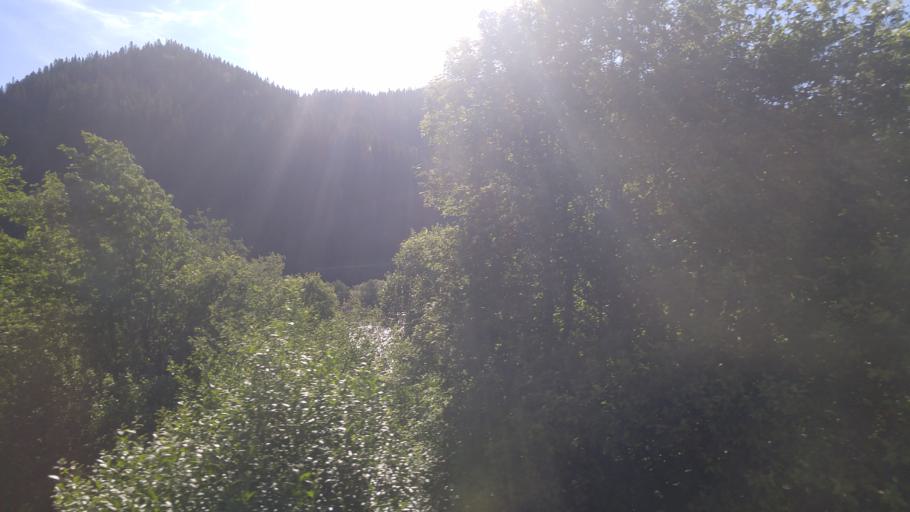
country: NO
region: Sor-Trondelag
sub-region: Melhus
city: Lundamo
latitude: 63.1937
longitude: 10.2974
